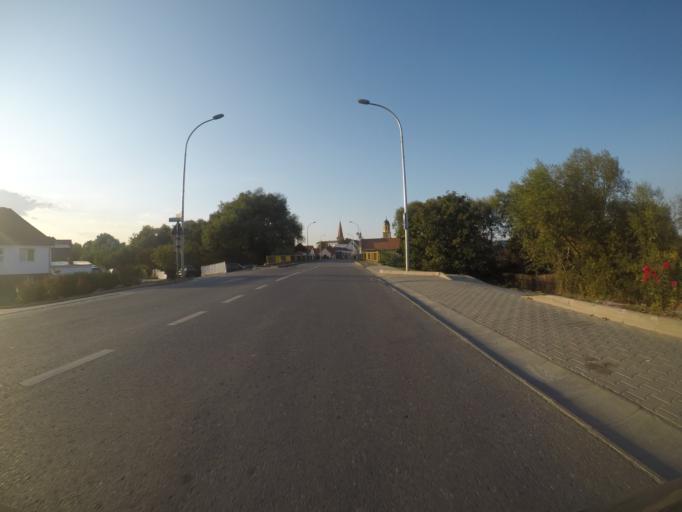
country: RO
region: Sibiu
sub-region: Comuna Selimbar
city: Selimbar
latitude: 45.7652
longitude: 24.1962
